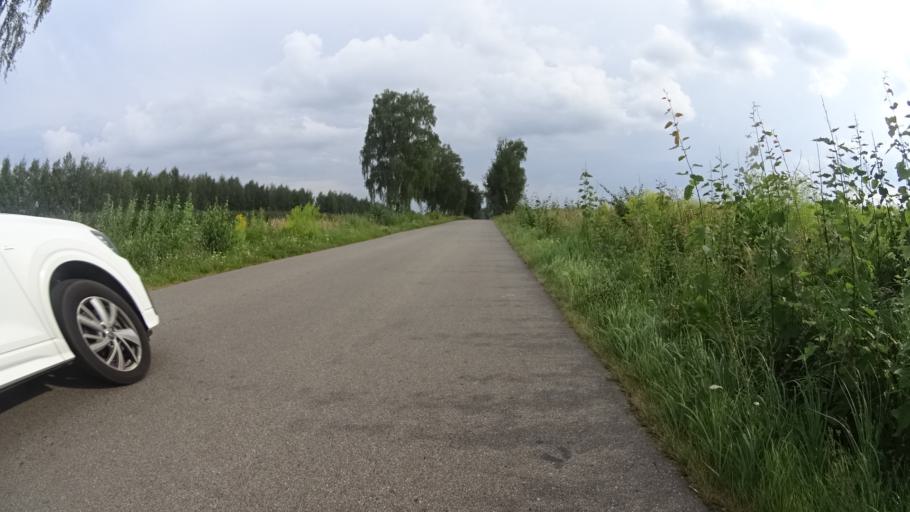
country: PL
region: Masovian Voivodeship
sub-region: Powiat grojecki
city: Goszczyn
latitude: 51.6951
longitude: 20.8565
